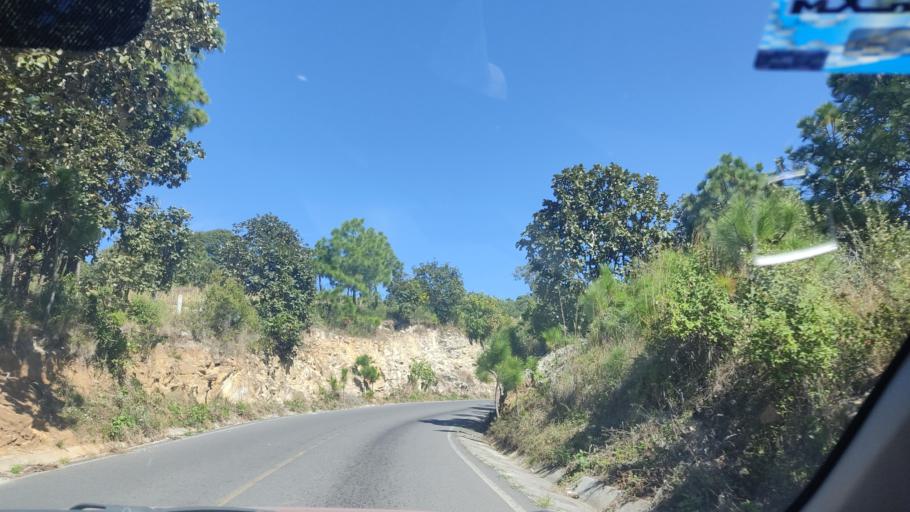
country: MX
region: Nayarit
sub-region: Jala
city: Rosa Blanca
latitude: 21.0996
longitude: -104.3671
